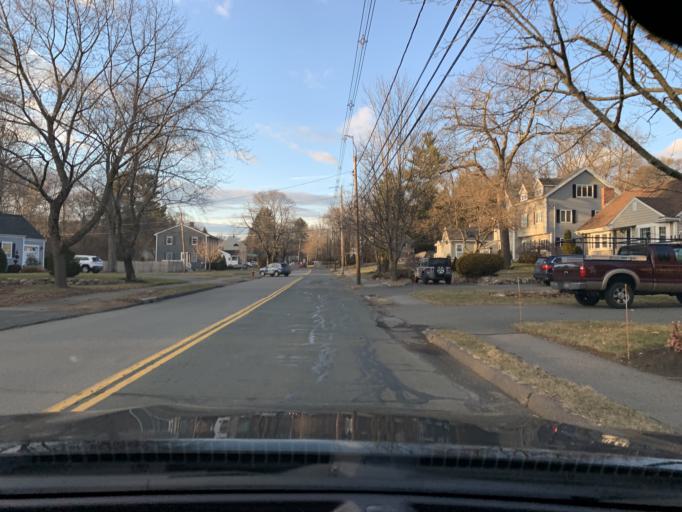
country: US
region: Massachusetts
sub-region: Essex County
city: Lynnfield
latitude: 42.5188
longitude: -71.0154
